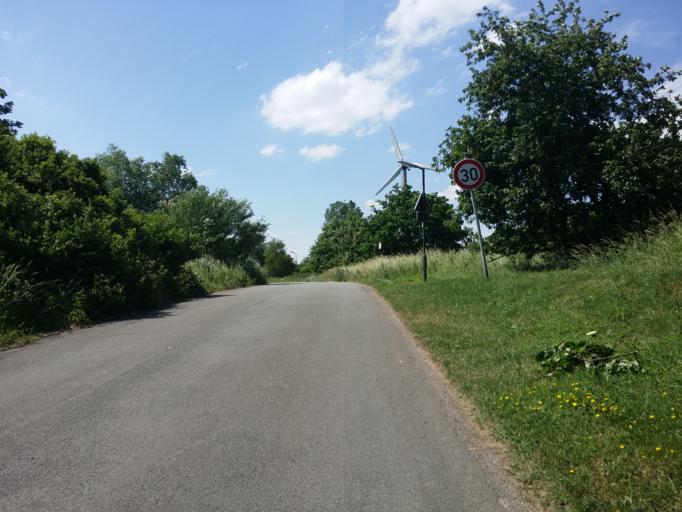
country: DE
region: Lower Saxony
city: Lemwerder
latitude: 53.1210
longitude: 8.6707
